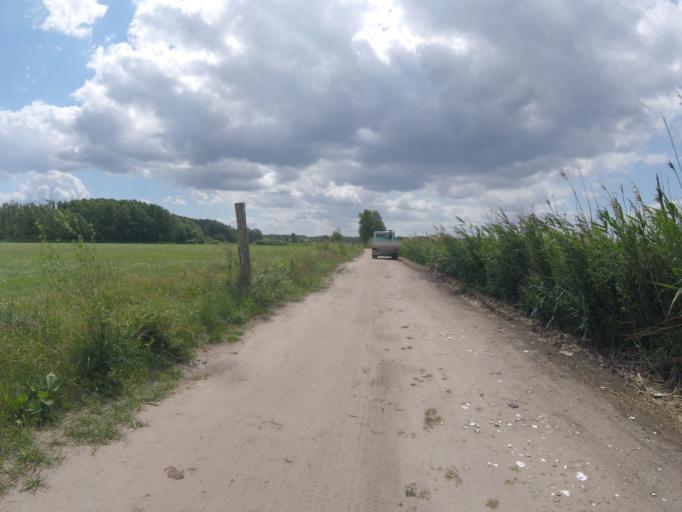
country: DE
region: Brandenburg
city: Bestensee
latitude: 52.2408
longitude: 13.6178
